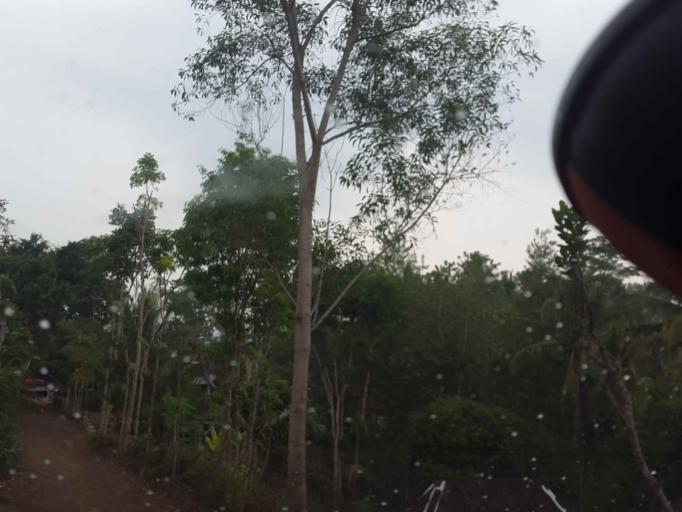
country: ID
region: East Java
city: Krajan Tengah
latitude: -7.9774
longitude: 111.3066
